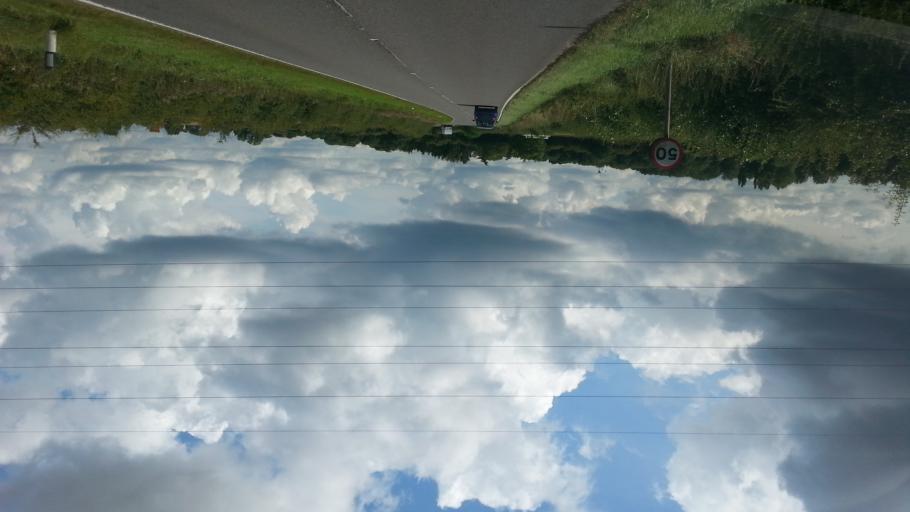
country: GB
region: England
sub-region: Nottinghamshire
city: Southwell
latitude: 53.0963
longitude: -0.9184
